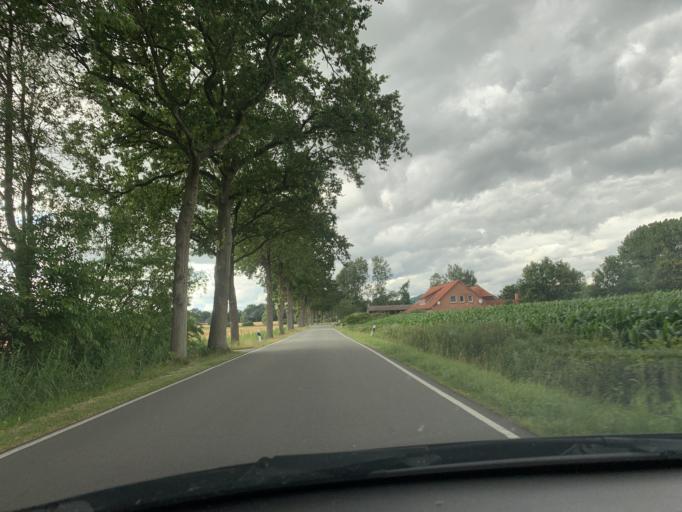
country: DE
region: Lower Saxony
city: Westerstede
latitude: 53.2217
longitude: 7.9065
